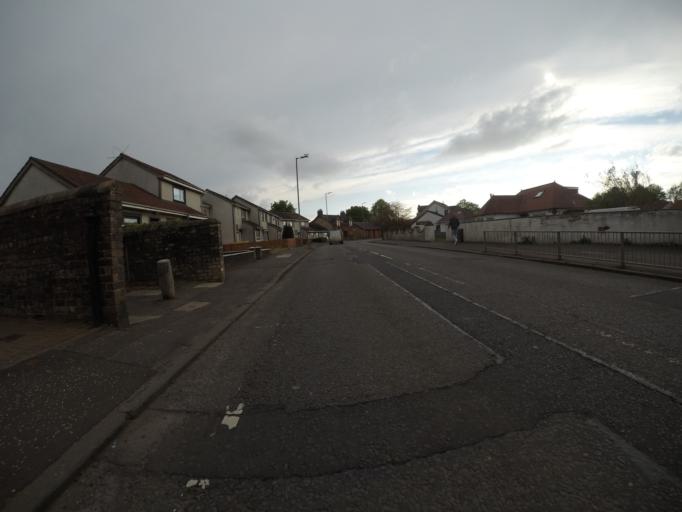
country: GB
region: Scotland
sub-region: North Ayrshire
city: Dreghorn
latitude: 55.6072
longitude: -4.6224
